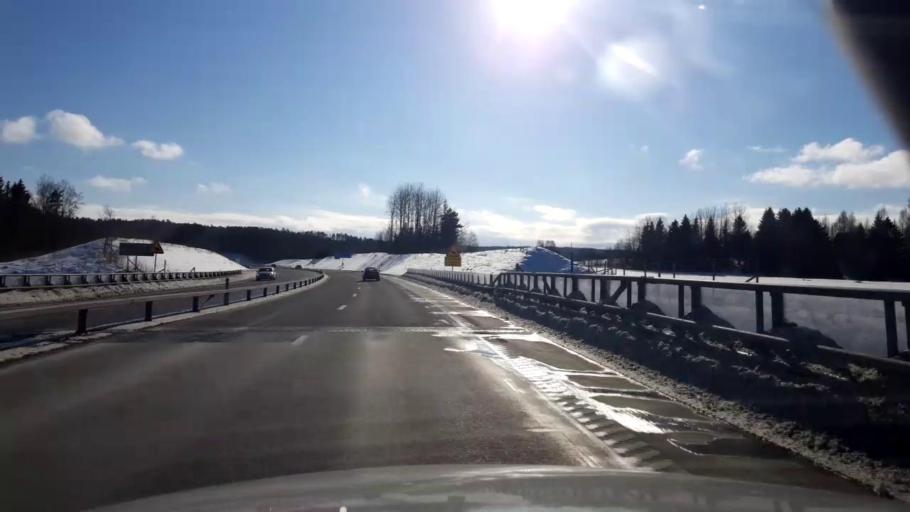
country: SE
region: Vaesternorrland
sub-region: Sundsvalls Kommun
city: Nolby
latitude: 62.2719
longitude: 17.3452
